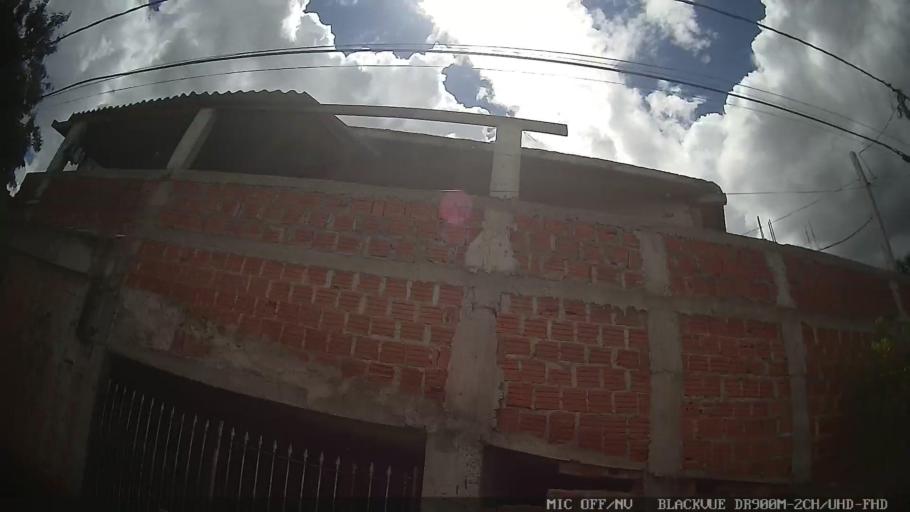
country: BR
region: Sao Paulo
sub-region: Jaguariuna
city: Jaguariuna
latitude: -22.6870
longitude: -46.9957
